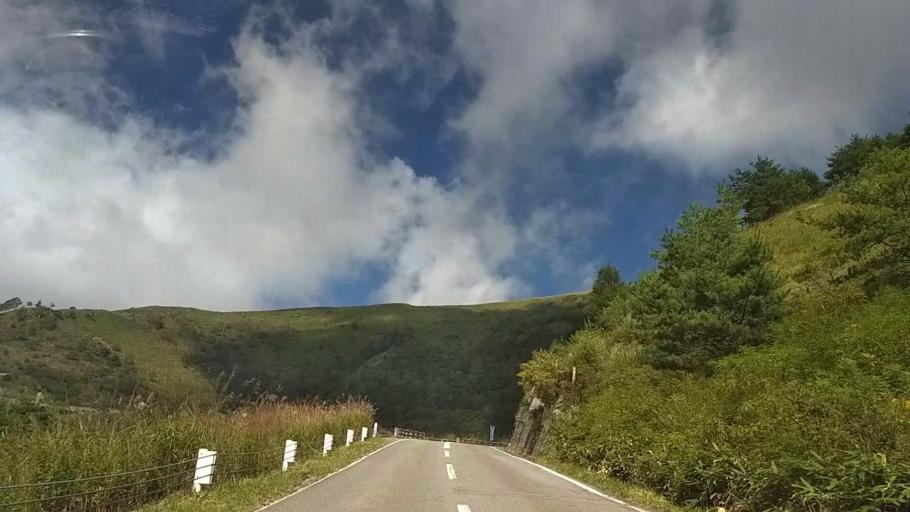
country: JP
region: Nagano
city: Suwa
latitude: 36.0960
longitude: 138.2020
